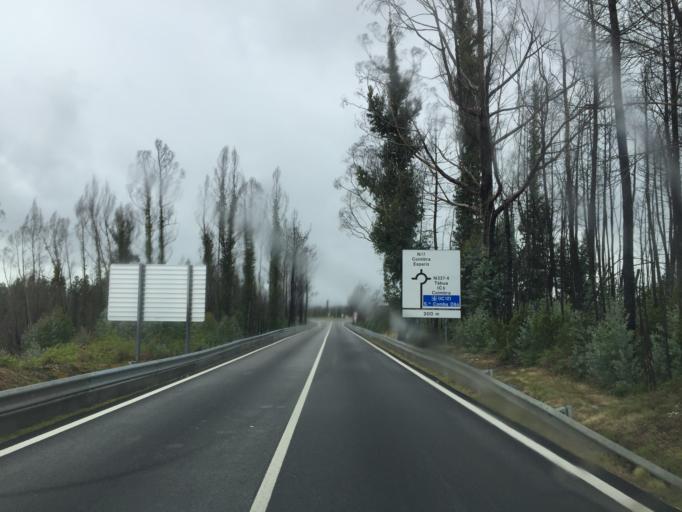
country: PT
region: Coimbra
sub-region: Tabua
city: Tabua
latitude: 40.3274
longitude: -7.9592
